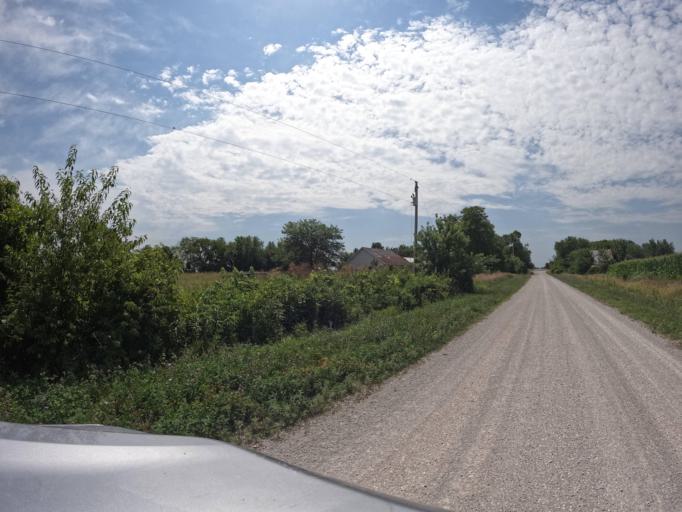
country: US
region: Iowa
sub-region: Appanoose County
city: Centerville
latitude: 40.8139
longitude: -92.9448
